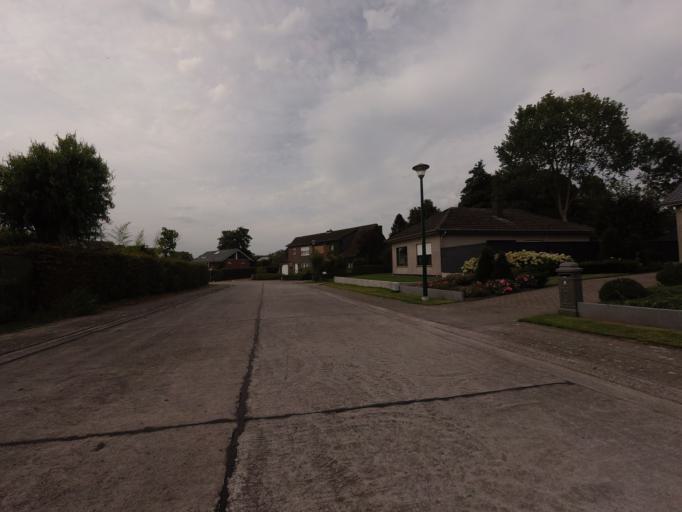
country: BE
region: Flanders
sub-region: Provincie Vlaams-Brabant
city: Meise
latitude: 50.9572
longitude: 4.3404
